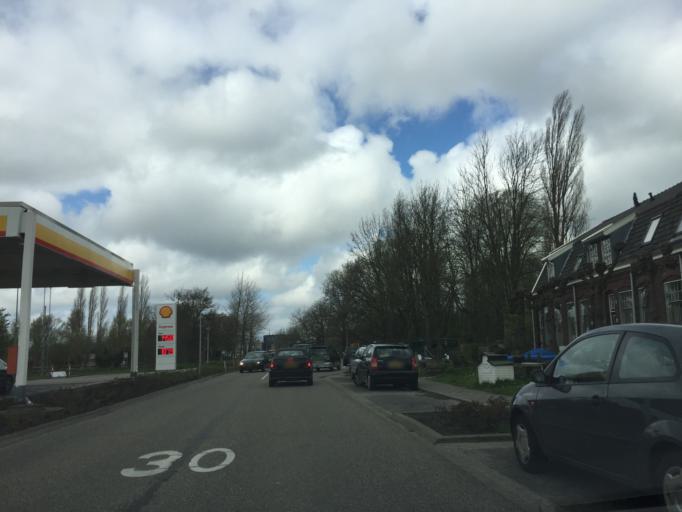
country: NL
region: South Holland
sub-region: Gemeente Leiderdorp
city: Leiderdorp
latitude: 52.1346
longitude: 4.5538
